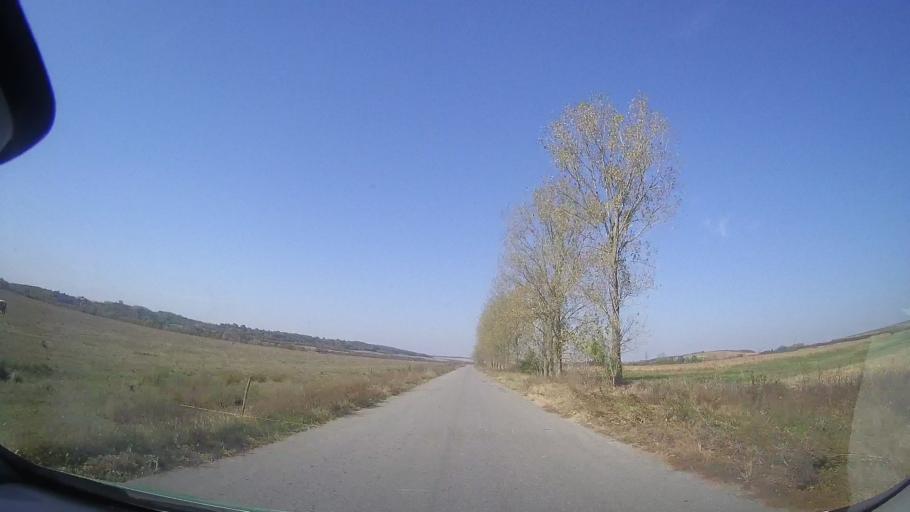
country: RO
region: Timis
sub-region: Comuna Ghizela
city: Ghizela
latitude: 45.8220
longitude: 21.7353
